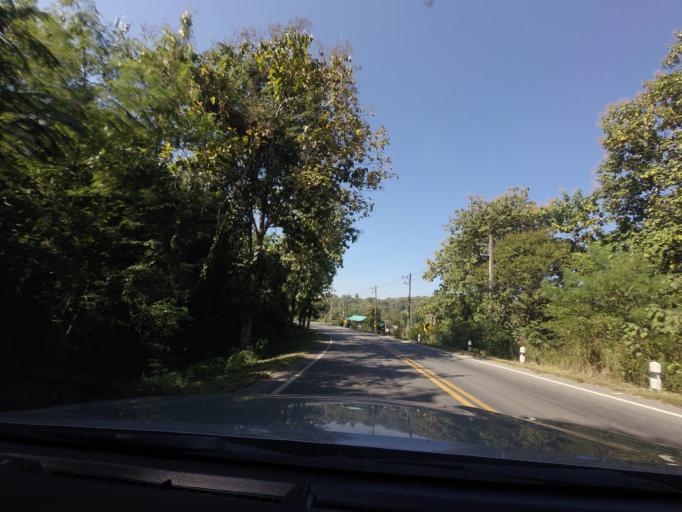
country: TH
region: Sukhothai
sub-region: Amphoe Si Satchanalai
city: Si Satchanalai
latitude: 17.6166
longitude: 99.7089
